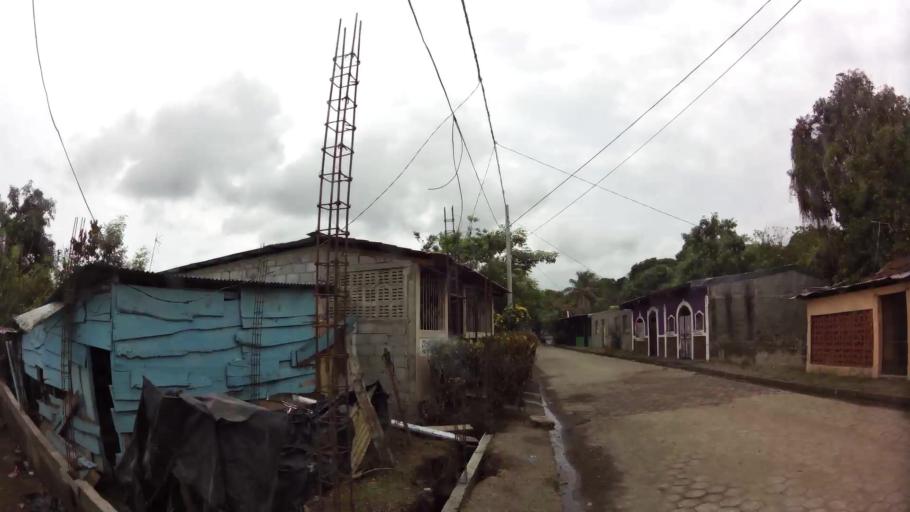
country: NI
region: Granada
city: Granada
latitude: 11.9363
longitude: -85.9451
